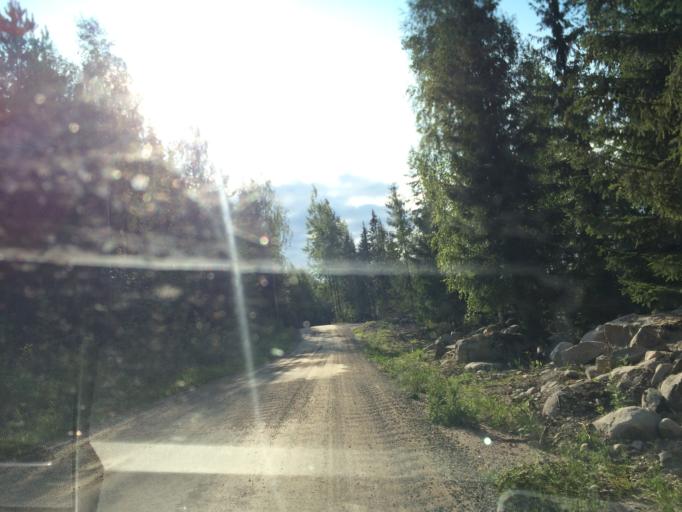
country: FI
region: Haeme
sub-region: Haemeenlinna
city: Renko
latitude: 60.9424
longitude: 24.3779
